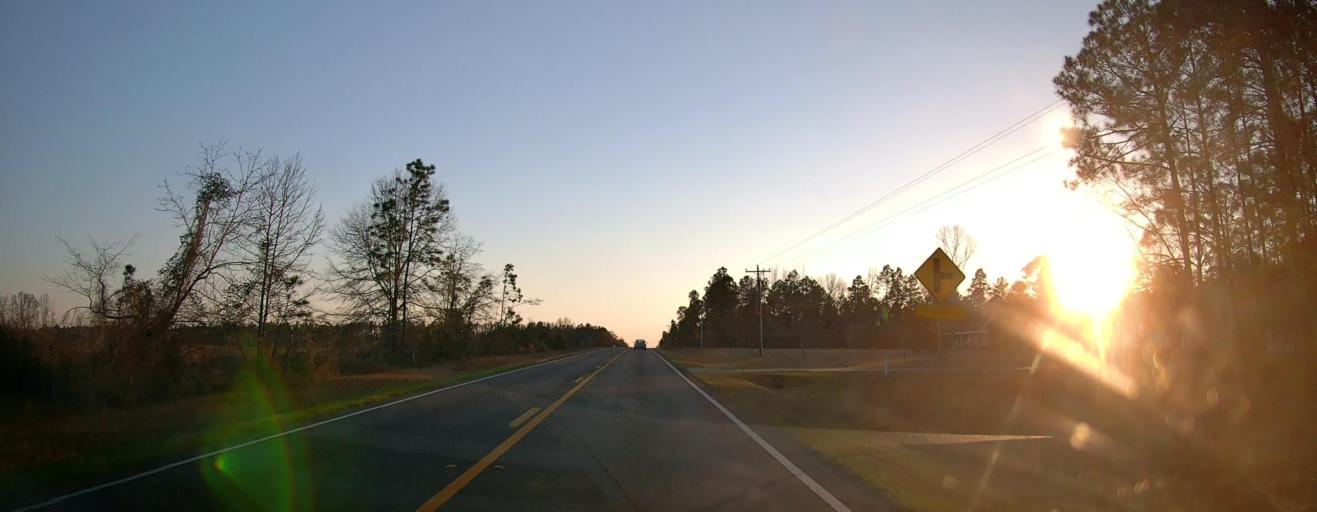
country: US
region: Georgia
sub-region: Laurens County
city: Dublin
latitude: 32.4114
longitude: -82.9595
